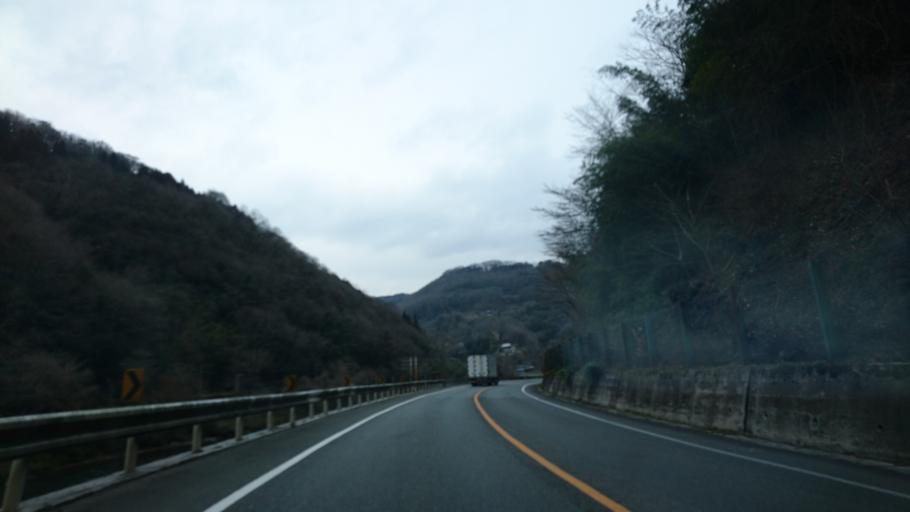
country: JP
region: Okayama
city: Niimi
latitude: 34.9145
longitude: 133.5213
